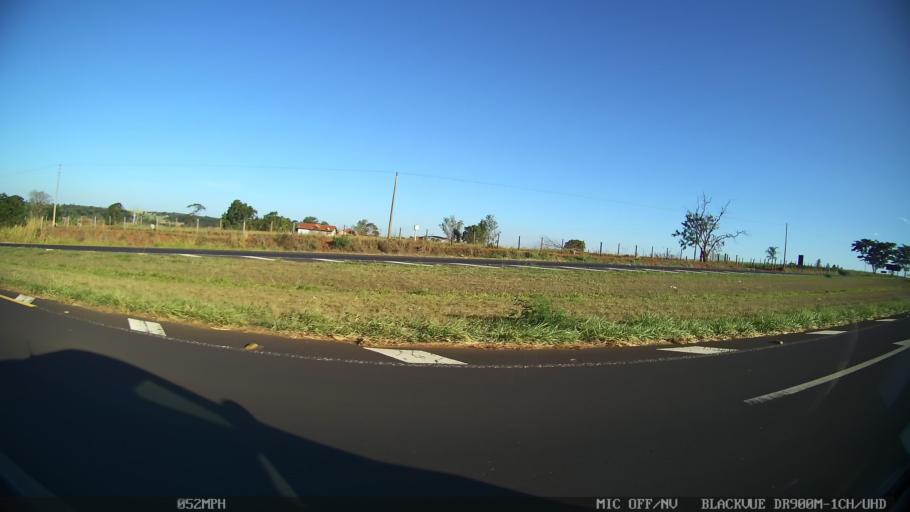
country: BR
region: Sao Paulo
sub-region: Guapiacu
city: Guapiacu
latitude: -20.7635
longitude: -49.1878
